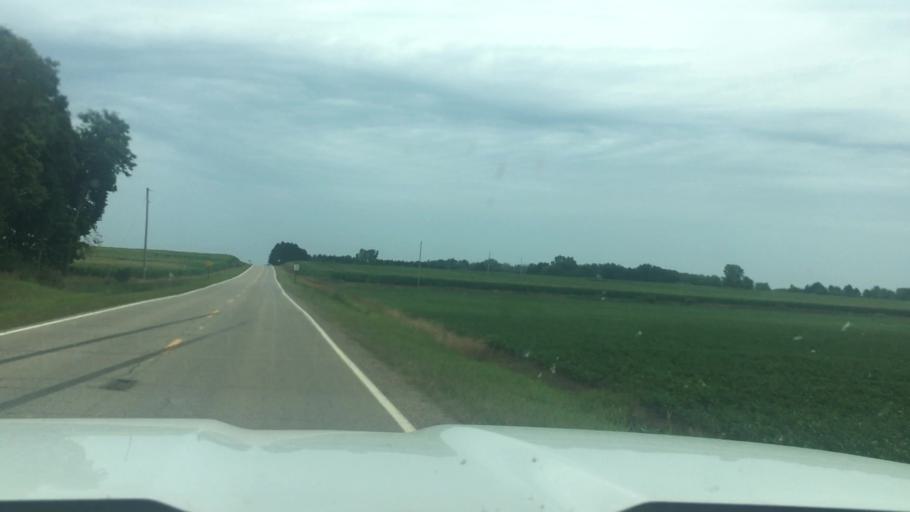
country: US
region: Michigan
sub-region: Clinton County
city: Saint Johns
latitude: 43.0326
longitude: -84.4843
